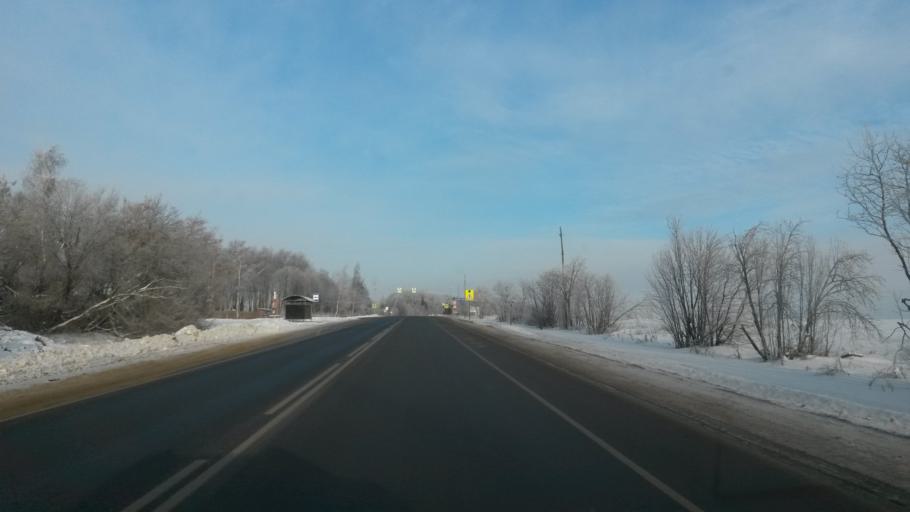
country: RU
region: Vladimir
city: Bogolyubovo
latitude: 56.2194
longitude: 40.4414
